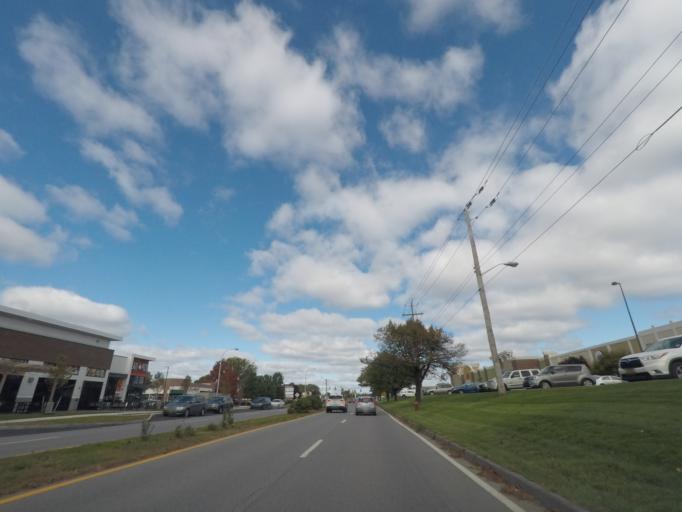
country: US
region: New York
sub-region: Saratoga County
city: Country Knolls
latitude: 42.8589
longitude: -73.7808
